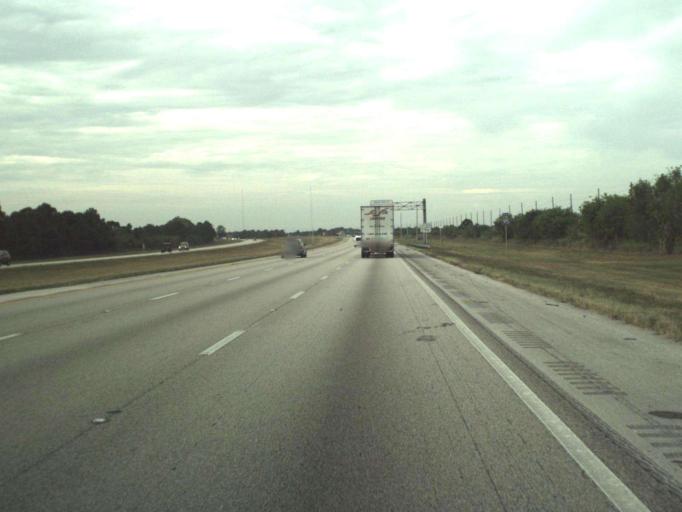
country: US
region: Florida
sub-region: Saint Lucie County
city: Port Saint Lucie
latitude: 27.2026
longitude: -80.4008
